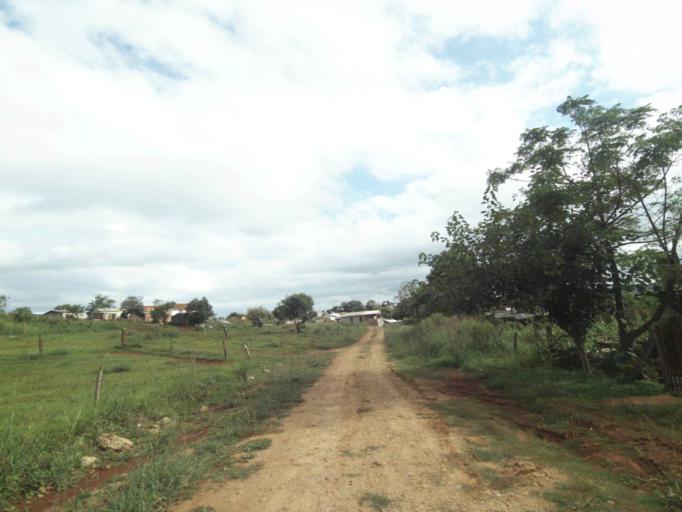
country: BR
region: Rio Grande do Sul
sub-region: Lagoa Vermelha
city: Lagoa Vermelha
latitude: -28.1962
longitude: -51.5271
